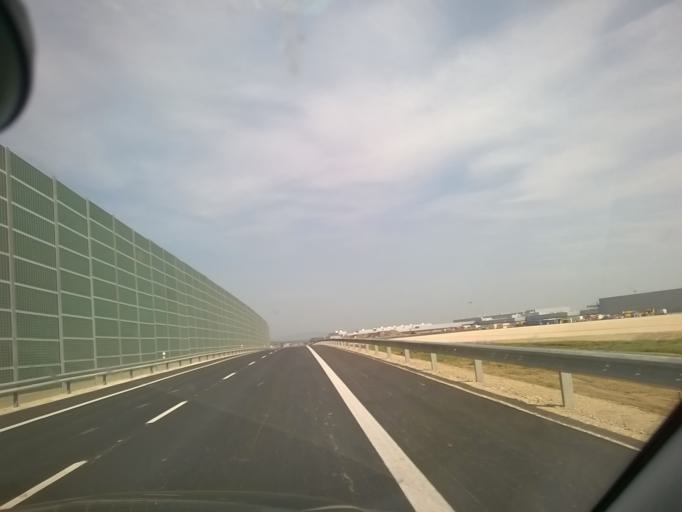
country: SK
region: Nitriansky
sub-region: Okres Nitra
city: Nitra
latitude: 48.3330
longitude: 18.0411
